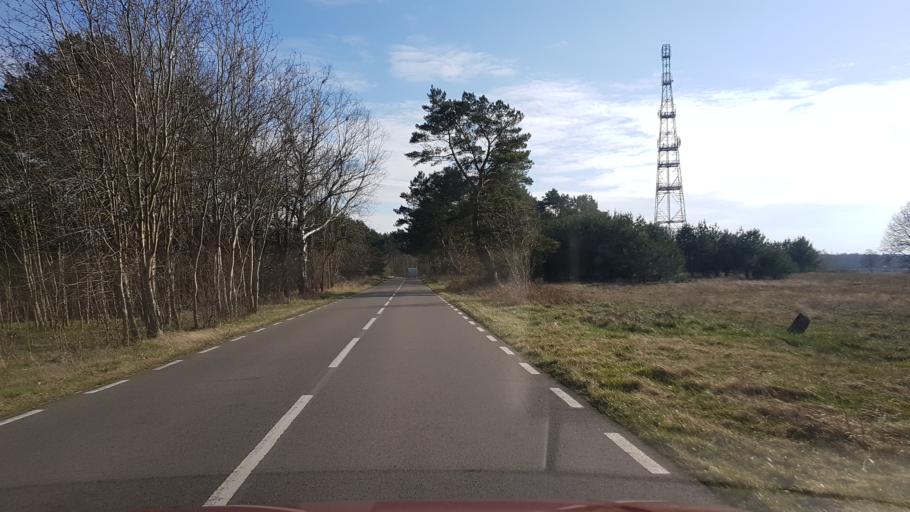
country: PL
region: West Pomeranian Voivodeship
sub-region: Powiat policki
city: Nowe Warpno
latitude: 53.7303
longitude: 14.3102
